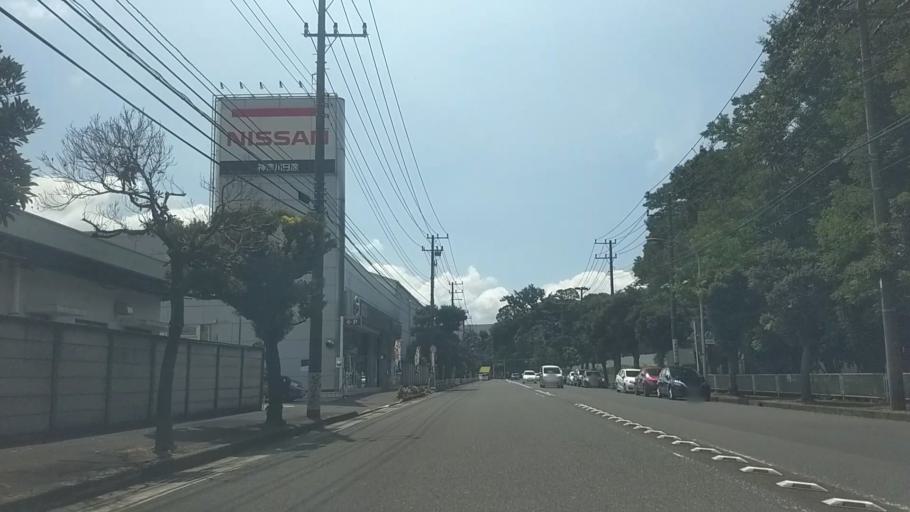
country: JP
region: Kanagawa
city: Yokosuka
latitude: 35.3189
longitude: 139.6363
